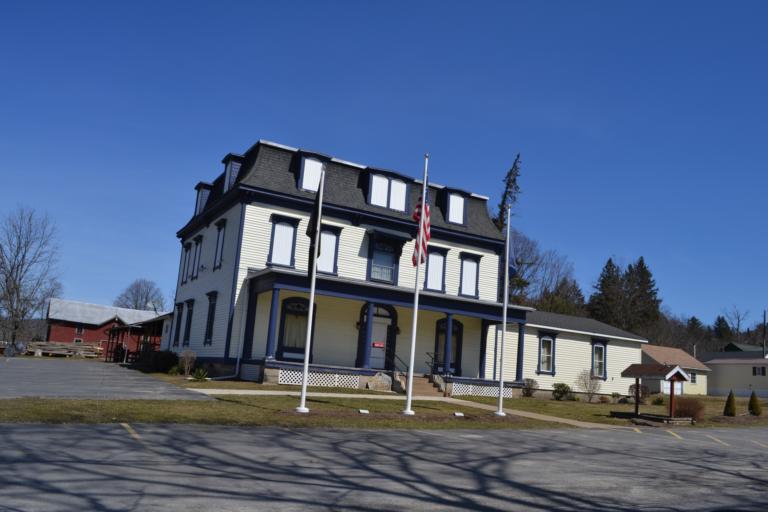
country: US
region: Pennsylvania
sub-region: Elk County
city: Johnsonburg
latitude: 41.5755
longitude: -78.6895
